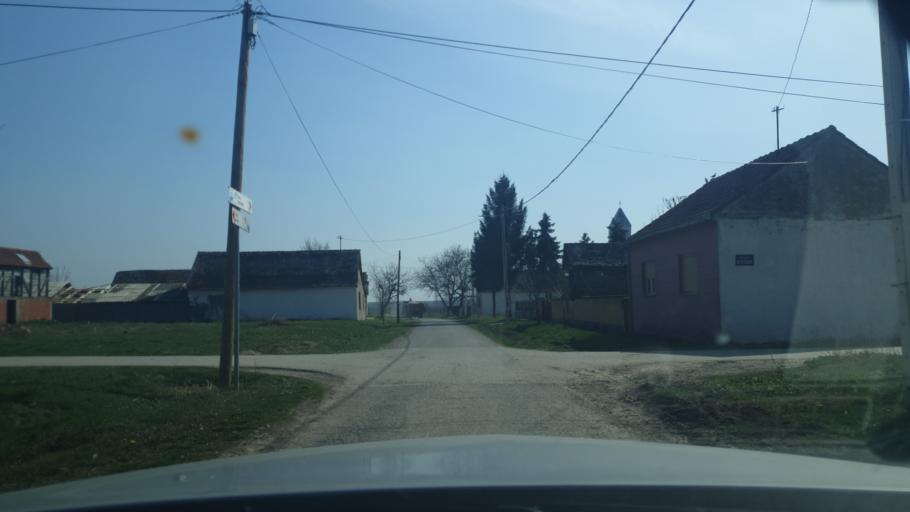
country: RS
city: Putinci
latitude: 45.0401
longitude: 19.9399
